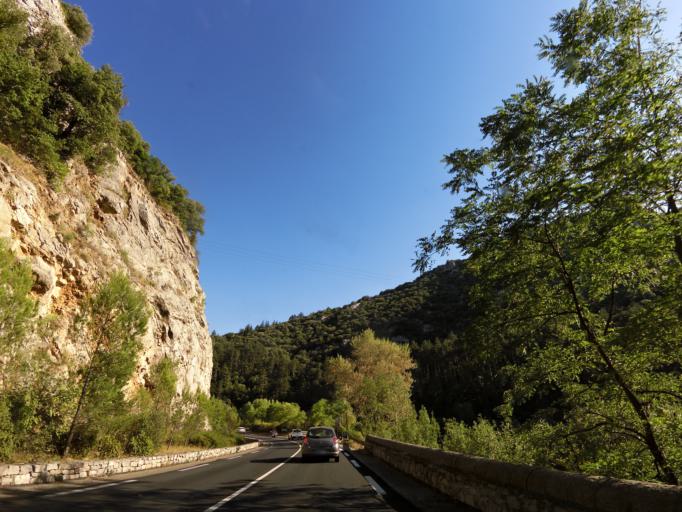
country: FR
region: Languedoc-Roussillon
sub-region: Departement de l'Herault
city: Ganges
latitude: 43.9396
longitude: 3.6903
